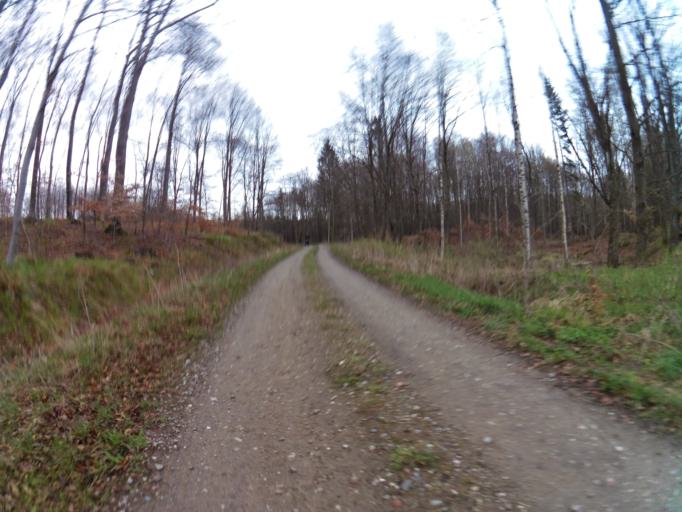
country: PL
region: West Pomeranian Voivodeship
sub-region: Powiat szczecinecki
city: Borne Sulinowo
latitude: 53.6562
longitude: 16.5171
